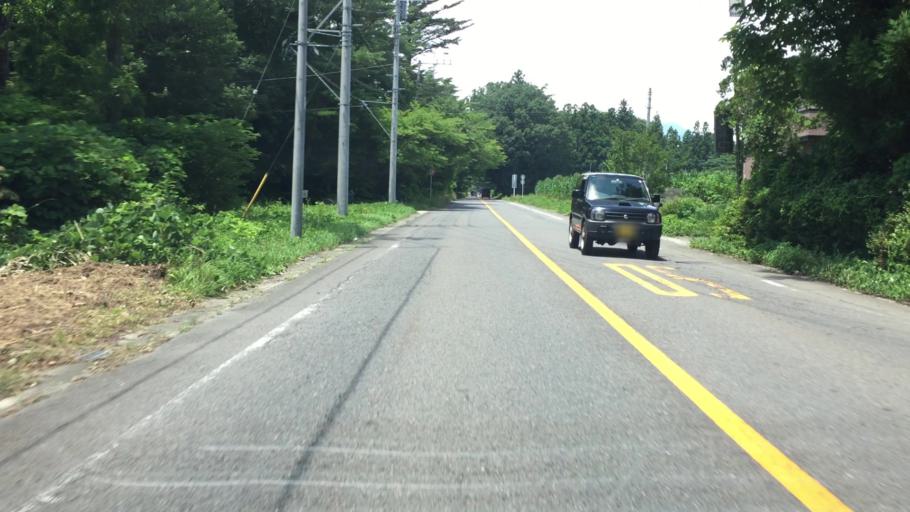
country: JP
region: Tochigi
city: Kuroiso
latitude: 37.0151
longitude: 139.9590
